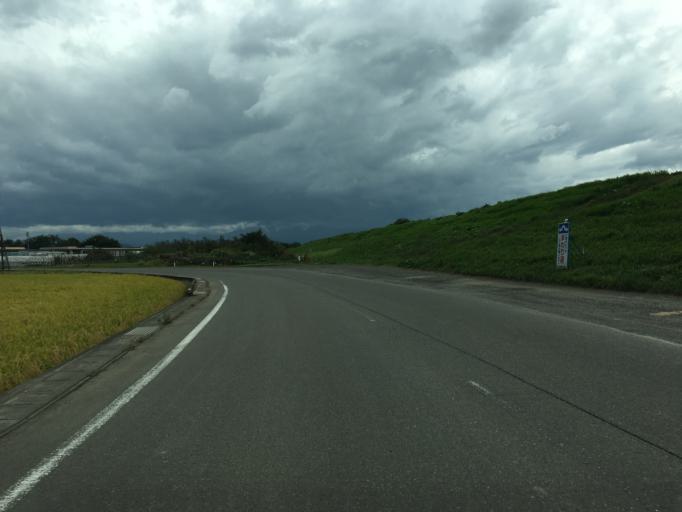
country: JP
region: Fukushima
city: Hobaramachi
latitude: 37.8384
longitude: 140.5502
